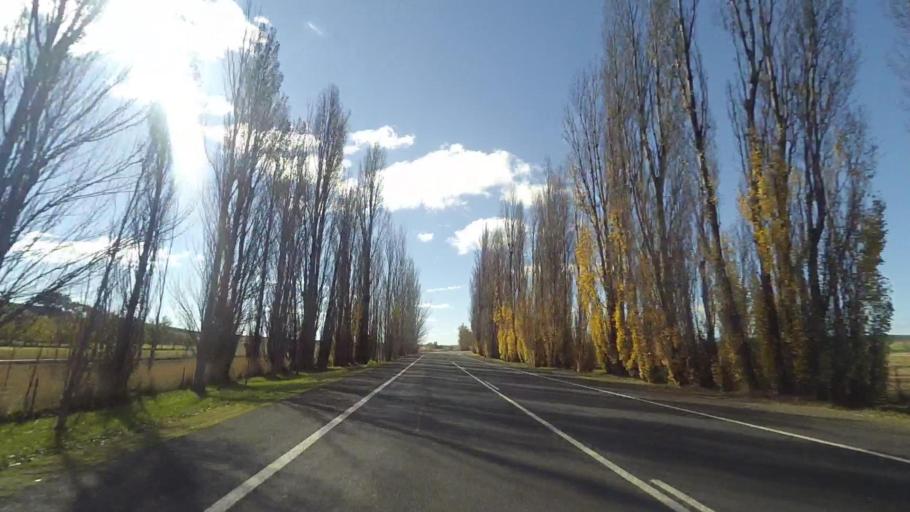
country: AU
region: New South Wales
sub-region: Bathurst Regional
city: Perthville
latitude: -33.4608
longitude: 149.5726
